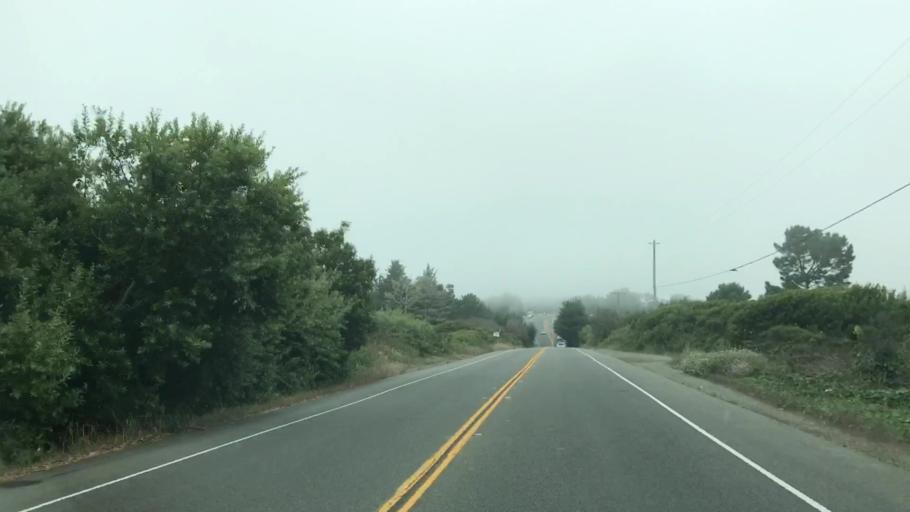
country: US
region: California
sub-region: San Mateo County
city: Colma
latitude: 37.6565
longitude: -122.4733
